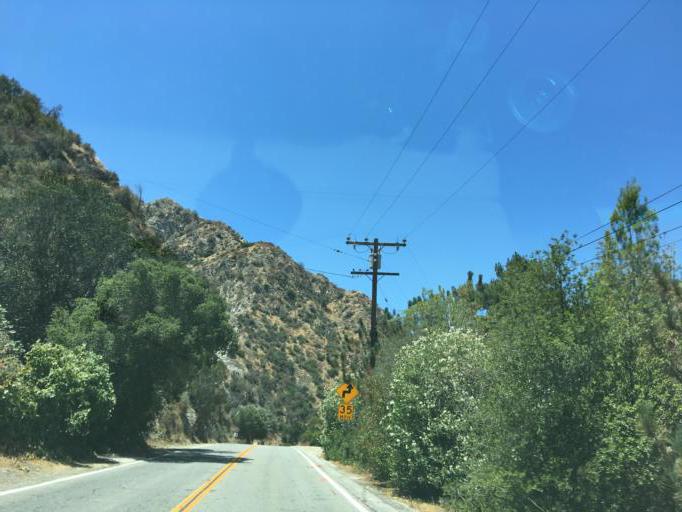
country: US
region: California
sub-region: Los Angeles County
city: La Crescenta-Montrose
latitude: 34.2998
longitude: -118.2727
